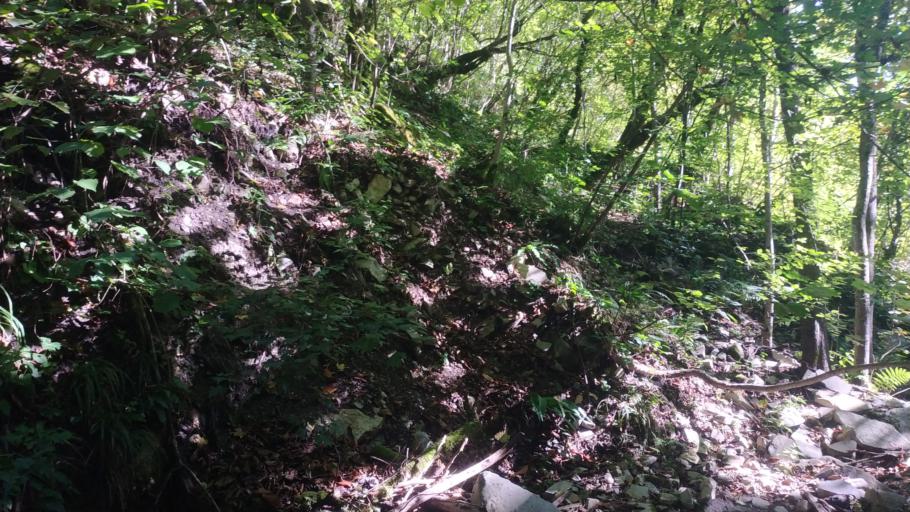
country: RU
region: Krasnodarskiy
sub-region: Sochi City
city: Lazarevskoye
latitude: 43.9838
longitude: 39.4117
